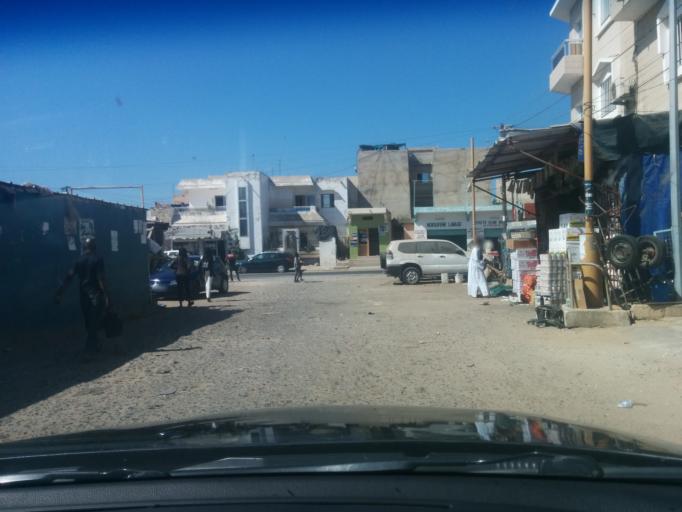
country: SN
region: Dakar
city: Grand Dakar
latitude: 14.7464
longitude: -17.4426
